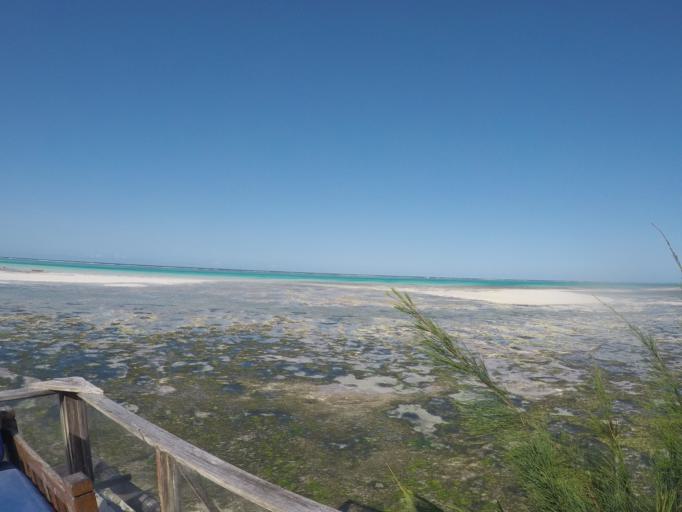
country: TZ
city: Kiwengwa
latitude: -6.1516
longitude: 39.5194
